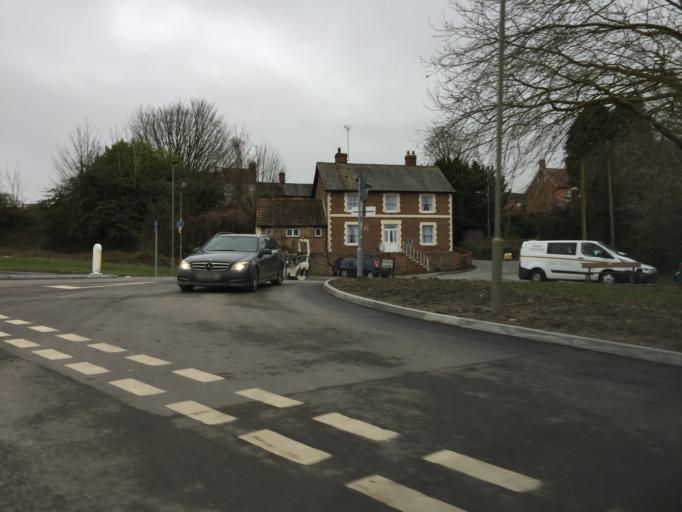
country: GB
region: England
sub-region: Oxfordshire
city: Wantage
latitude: 51.5897
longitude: -1.4518
